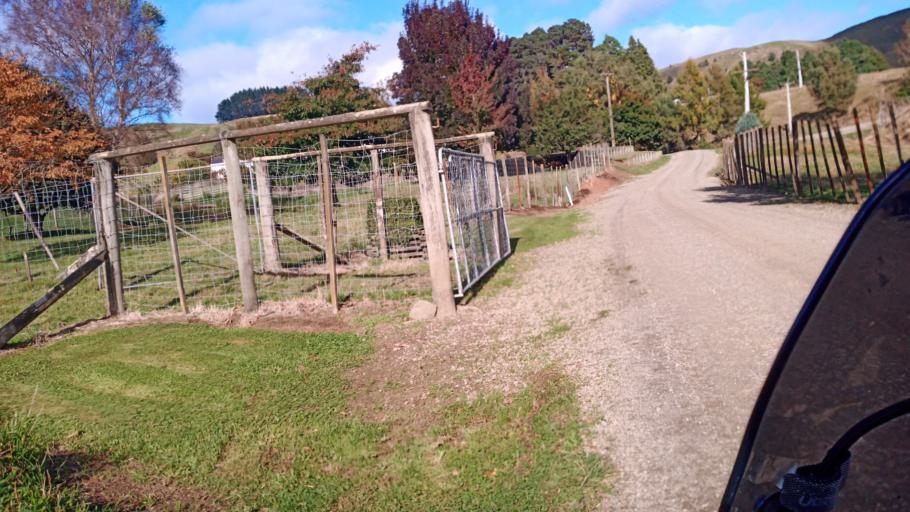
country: NZ
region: Bay of Plenty
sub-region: Opotiki District
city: Opotiki
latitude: -38.4614
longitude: 177.3842
